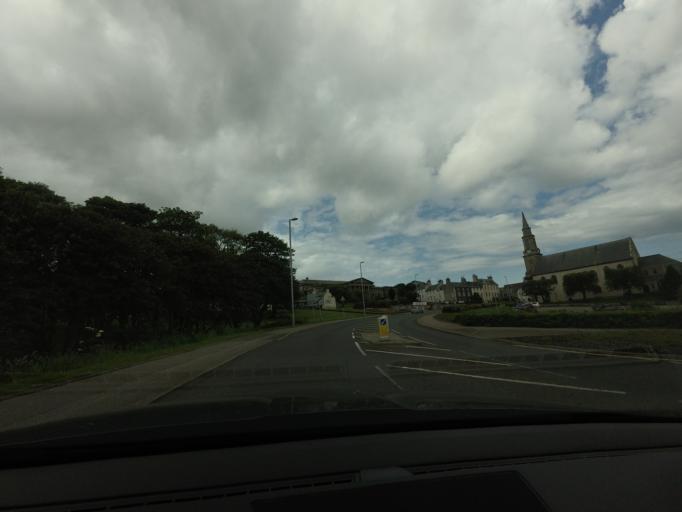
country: GB
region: Scotland
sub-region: Aberdeenshire
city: Banff
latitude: 57.6619
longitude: -2.5226
